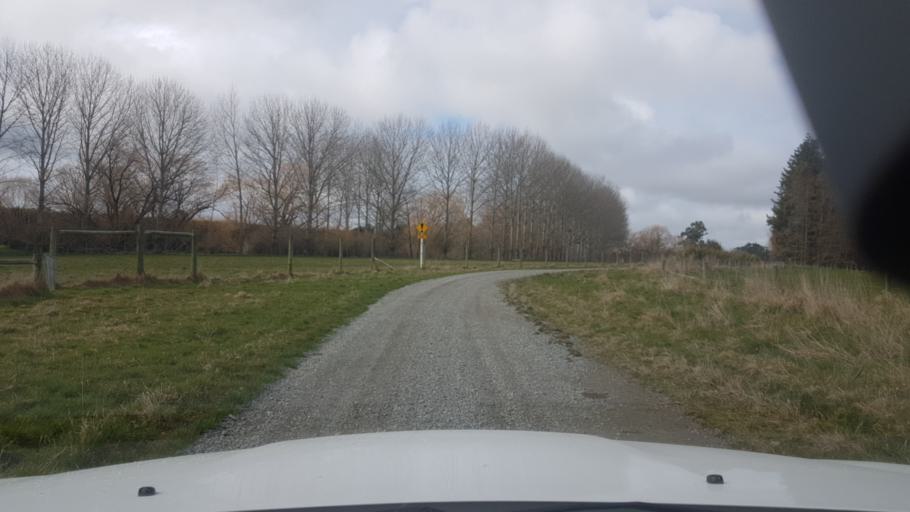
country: NZ
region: Canterbury
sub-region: Timaru District
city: Pleasant Point
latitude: -44.0117
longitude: 171.2156
